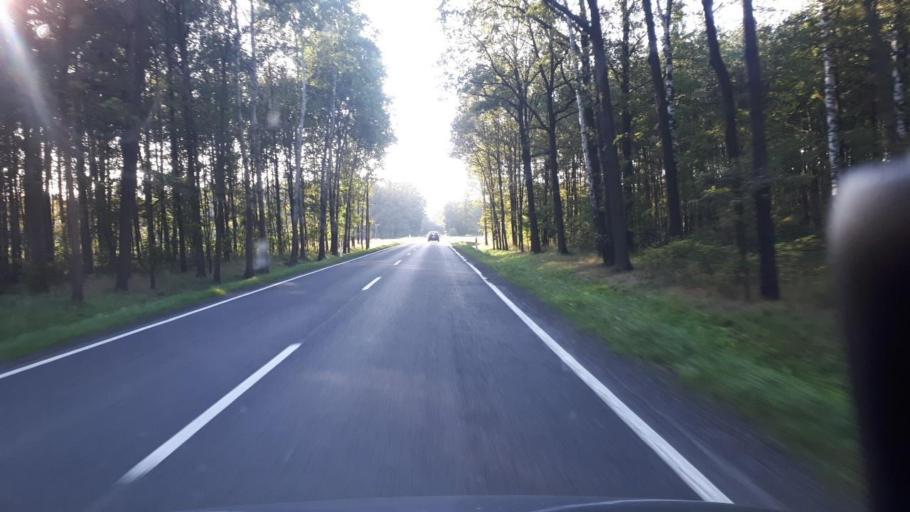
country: PL
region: Opole Voivodeship
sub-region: Powiat oleski
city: Olesno
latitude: 50.8461
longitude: 18.4839
